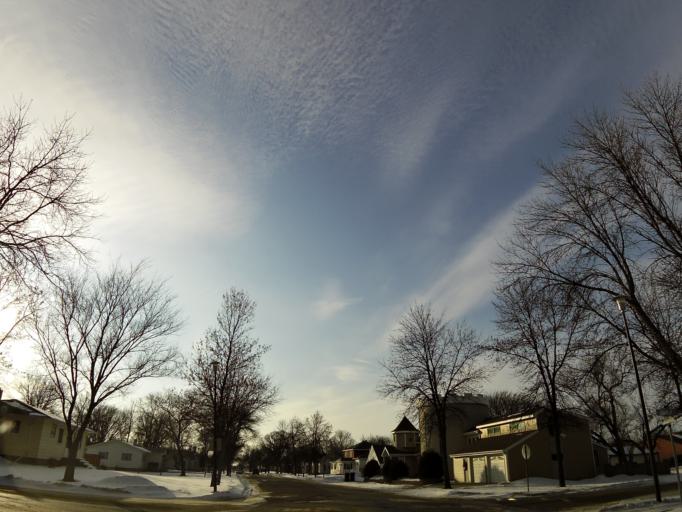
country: US
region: North Dakota
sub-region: Walsh County
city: Grafton
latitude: 48.4194
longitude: -97.3992
